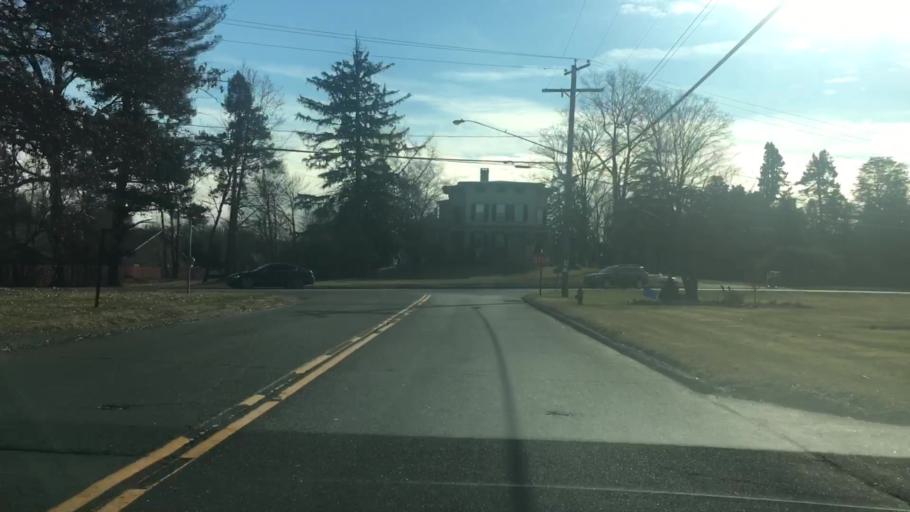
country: US
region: Connecticut
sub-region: Middlesex County
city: Middletown
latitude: 41.5329
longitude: -72.6496
